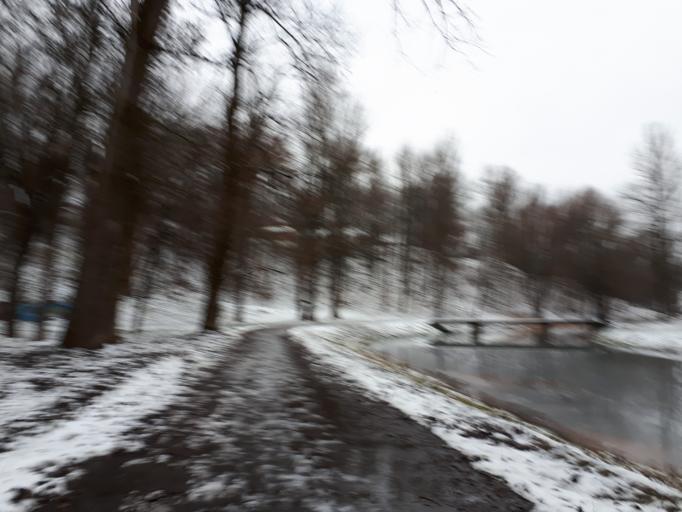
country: BY
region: Vitebsk
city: Vitebsk
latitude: 55.1984
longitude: 30.2113
